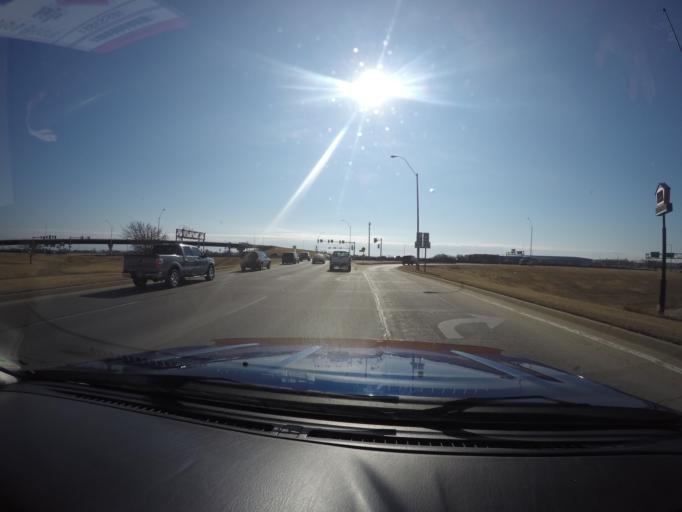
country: US
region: Kansas
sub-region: Sedgwick County
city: Wichita
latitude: 37.6736
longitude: -97.4288
